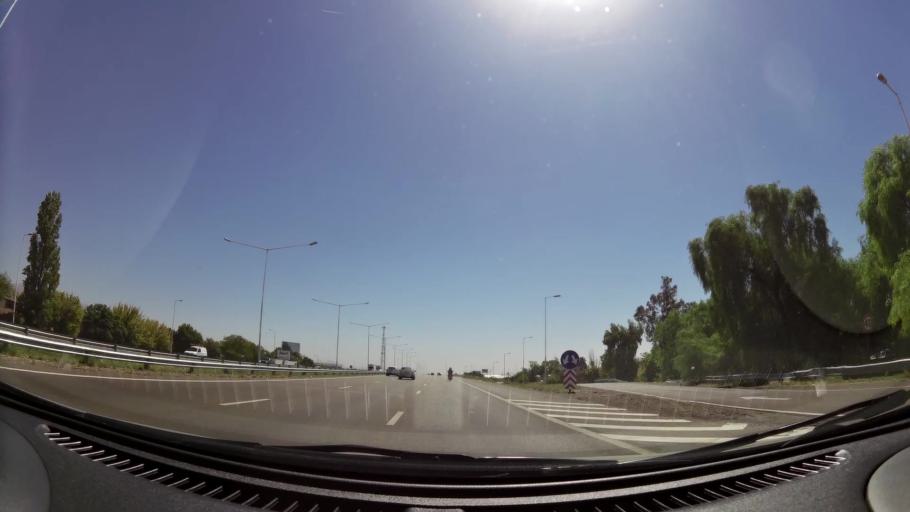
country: AR
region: Mendoza
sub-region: Departamento de Godoy Cruz
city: Godoy Cruz
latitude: -32.9434
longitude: -68.8311
